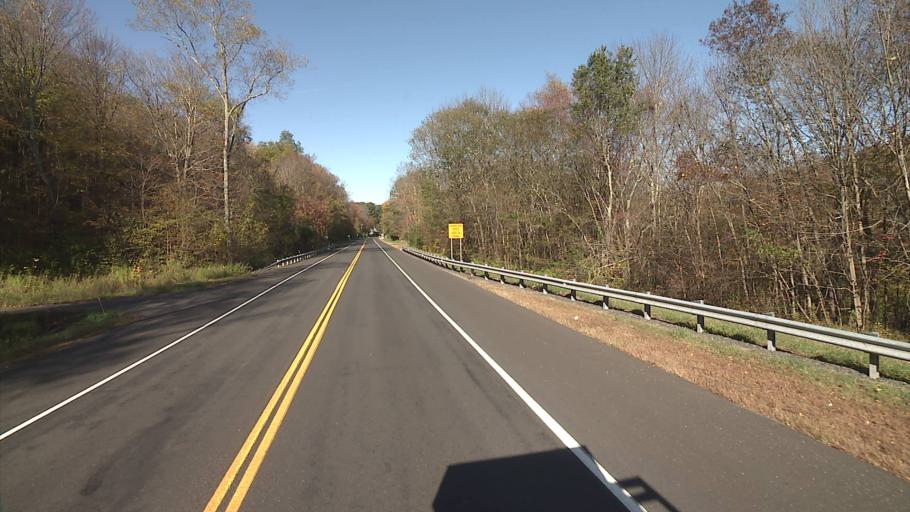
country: US
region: Connecticut
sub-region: Tolland County
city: Coventry Lake
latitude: 41.7710
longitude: -72.4095
